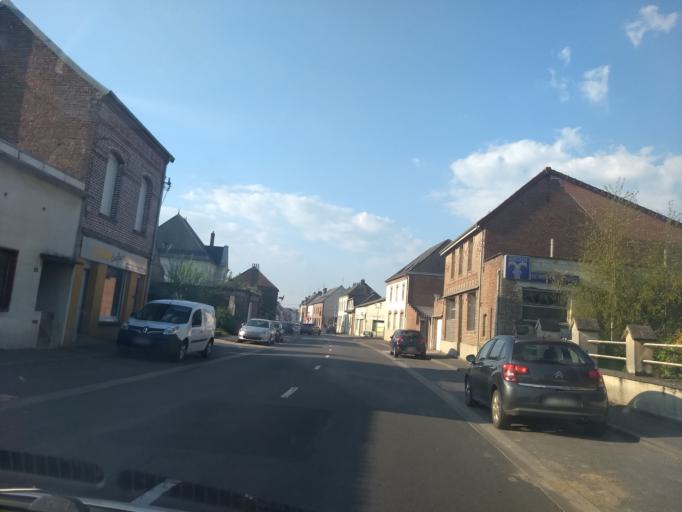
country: FR
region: Nord-Pas-de-Calais
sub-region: Departement du Pas-de-Calais
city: Bucquoy
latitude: 50.1414
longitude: 2.7099
